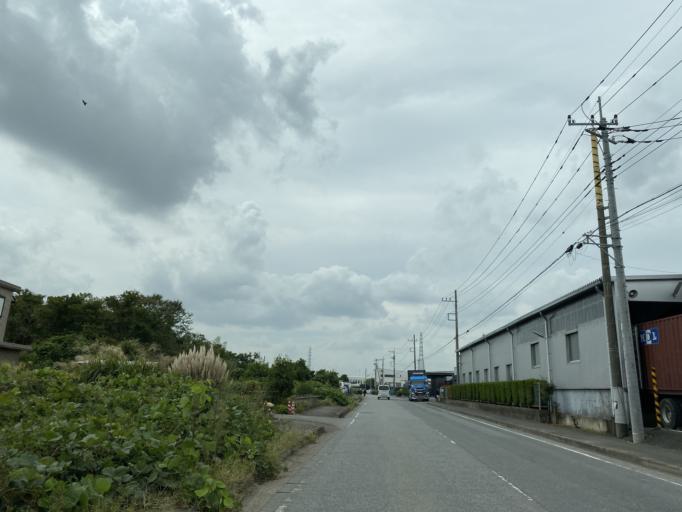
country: JP
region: Ibaraki
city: Mitsukaido
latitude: 36.0285
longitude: 140.0472
